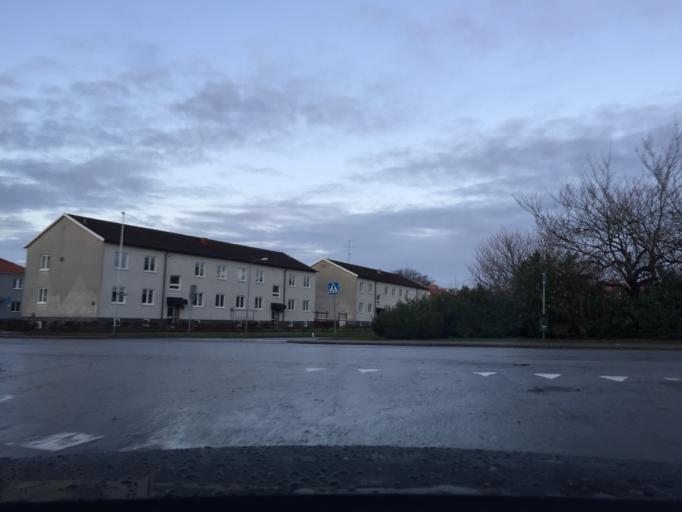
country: SE
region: Blekinge
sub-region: Karlshamns Kommun
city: Karlshamn
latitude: 56.1746
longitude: 14.8670
